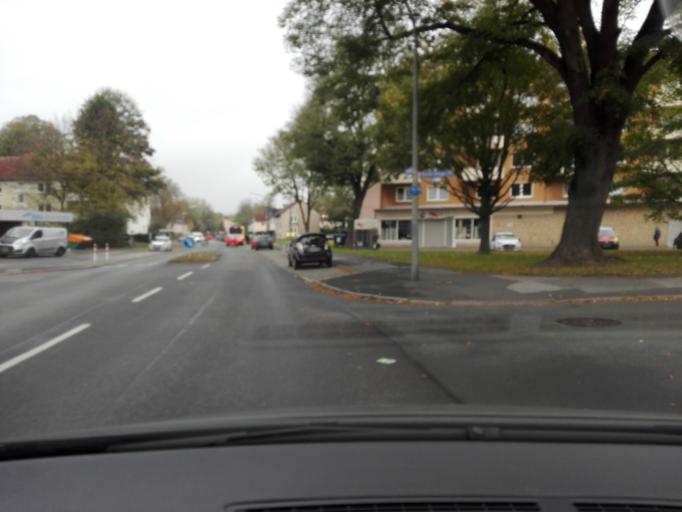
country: DE
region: North Rhine-Westphalia
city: Lanstrop
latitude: 51.5292
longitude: 7.5399
